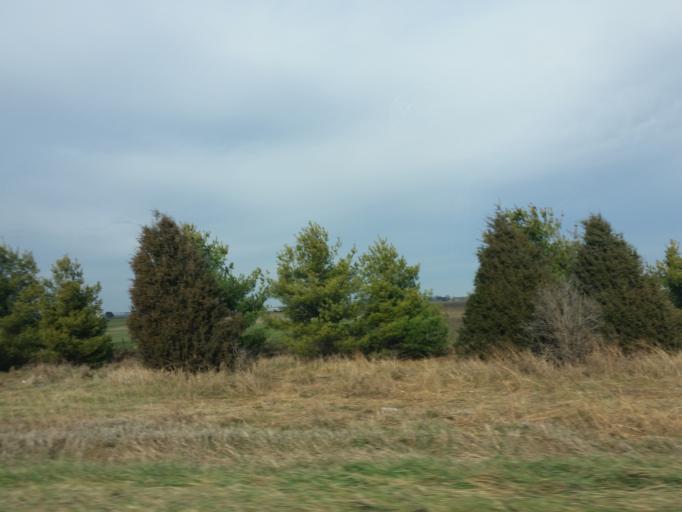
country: US
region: Iowa
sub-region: Scott County
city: Eldridge
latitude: 41.6022
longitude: -90.6507
